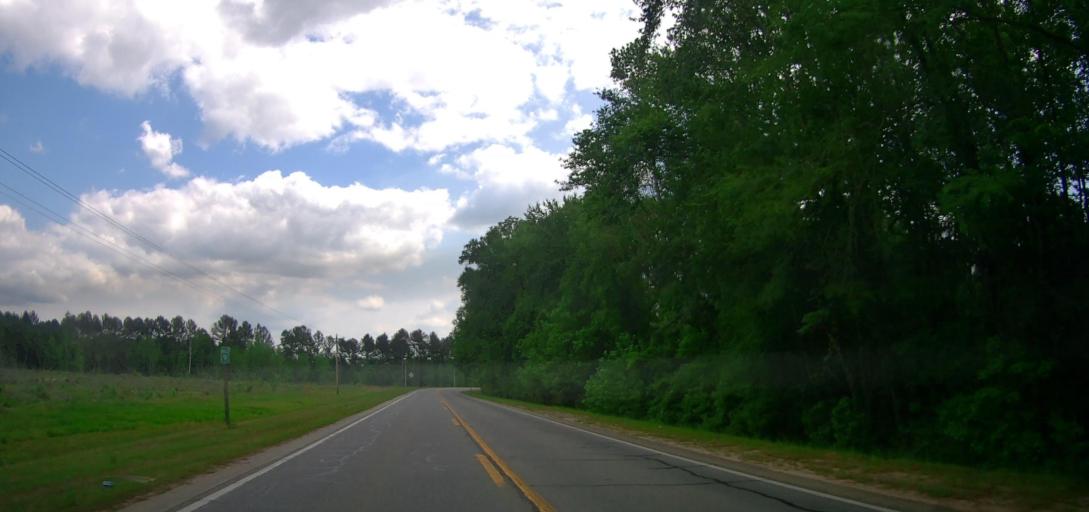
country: US
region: Georgia
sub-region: Laurens County
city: East Dublin
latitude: 32.4809
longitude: -82.8182
